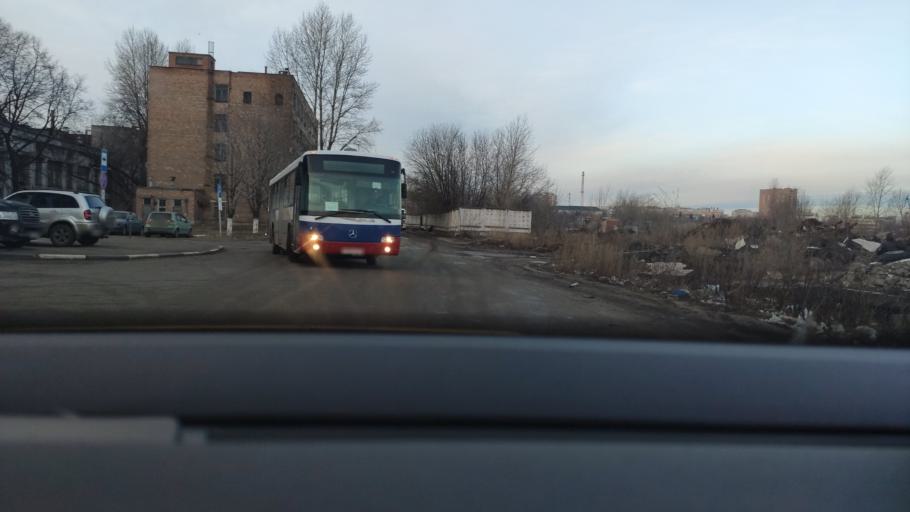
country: RU
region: Moskovskaya
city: Kozhukhovo
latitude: 55.6889
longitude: 37.6403
